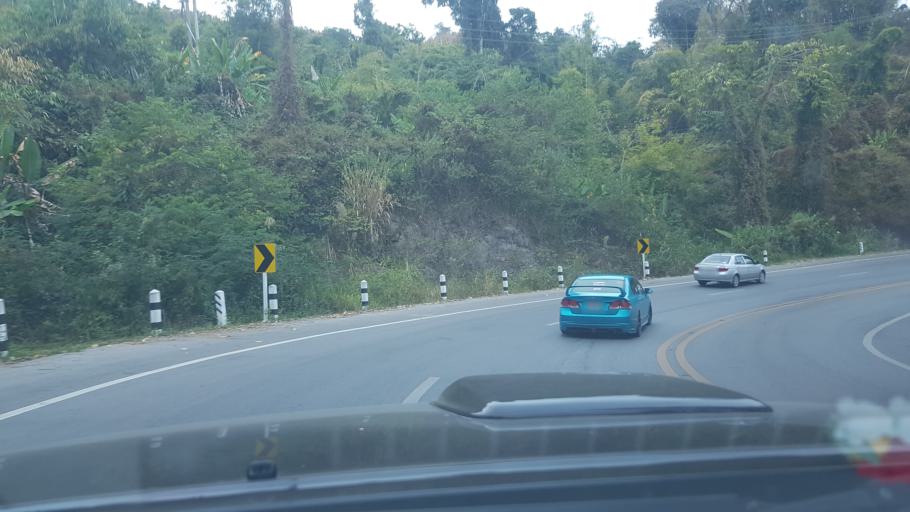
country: TH
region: Phetchabun
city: Khao Kho
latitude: 16.5478
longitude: 101.0335
